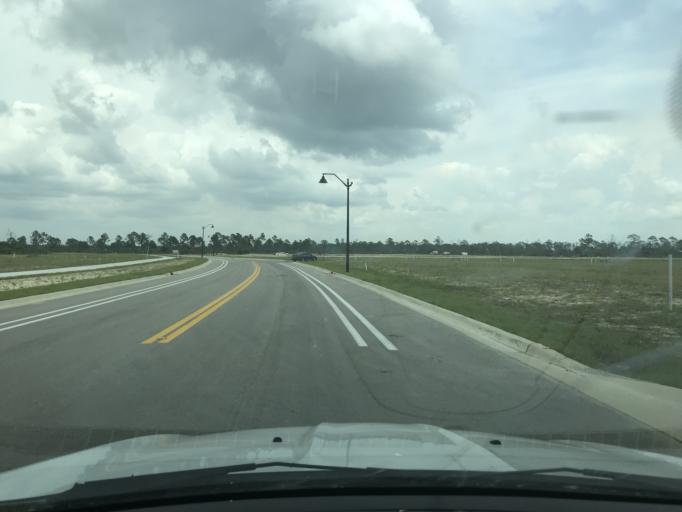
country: US
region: Florida
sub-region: Lee County
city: Olga
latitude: 26.7894
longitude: -81.7356
